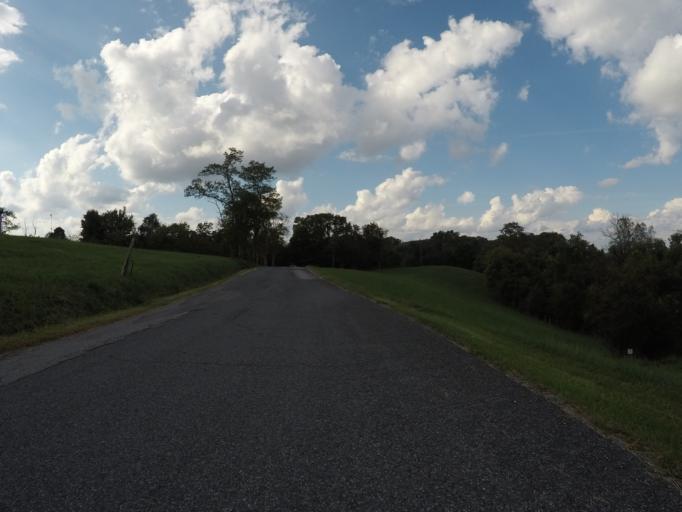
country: US
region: West Virginia
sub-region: Wayne County
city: Lavalette
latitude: 38.3604
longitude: -82.4658
